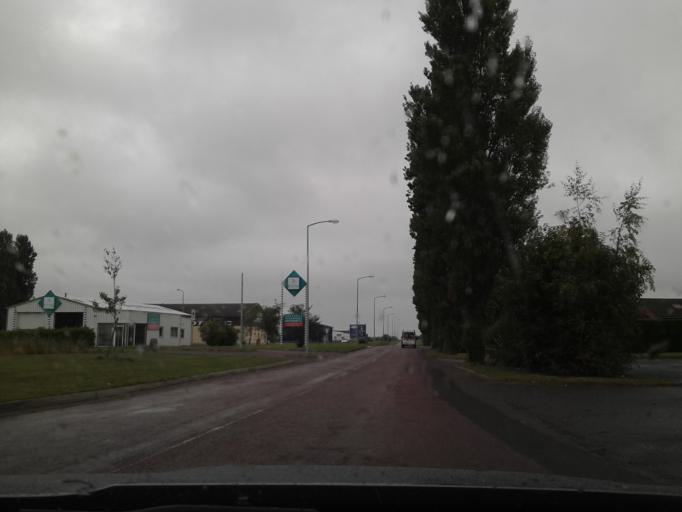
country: FR
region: Lower Normandy
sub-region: Departement de la Manche
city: Carentan
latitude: 49.3125
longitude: -1.2568
